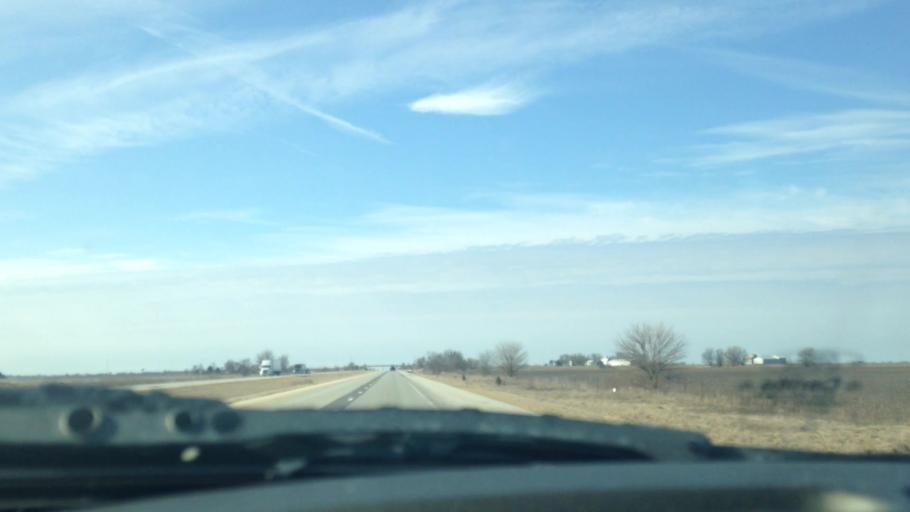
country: US
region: Illinois
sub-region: Ford County
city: Paxton
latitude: 40.4994
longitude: -88.0897
